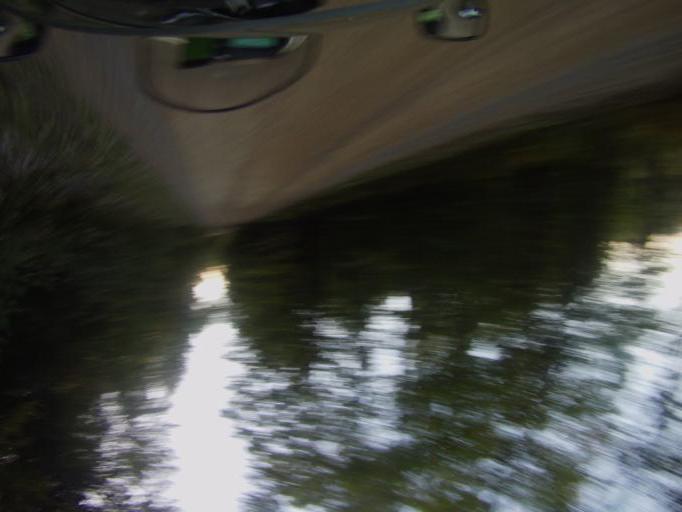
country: US
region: Vermont
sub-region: Addison County
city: Middlebury (village)
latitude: 43.9954
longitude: -73.0425
